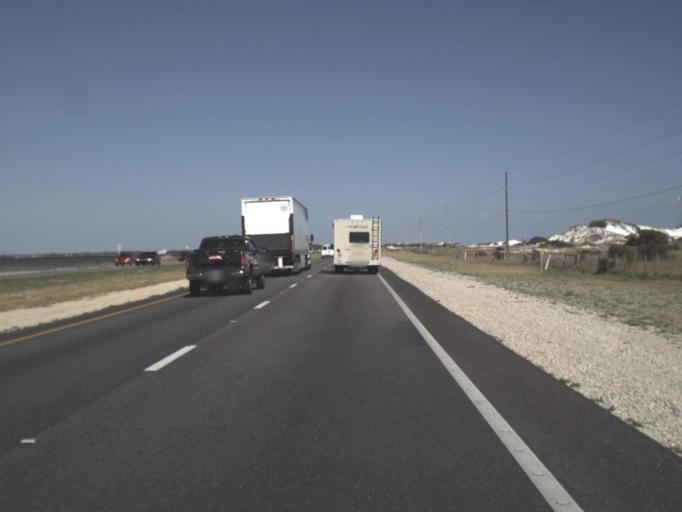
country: US
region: Florida
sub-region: Okaloosa County
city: Lake Lorraine
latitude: 30.3947
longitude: -86.5670
